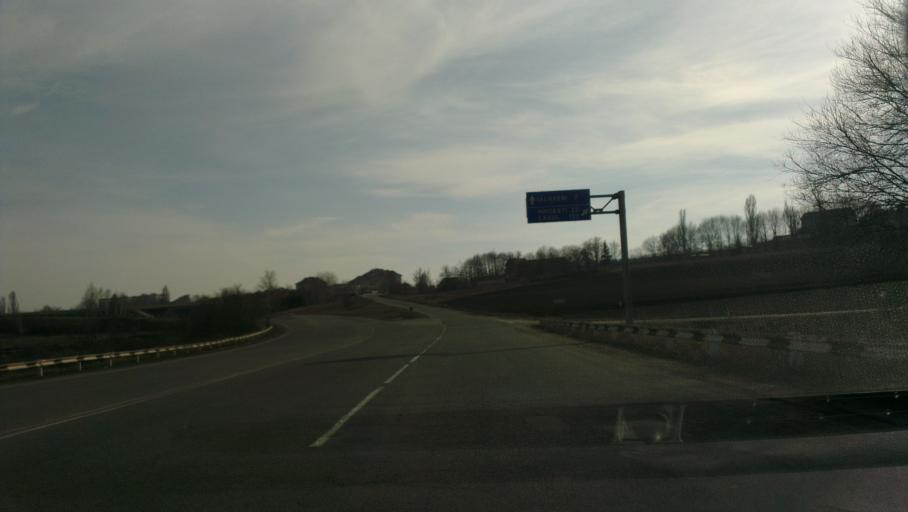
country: MD
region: Laloveni
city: Ialoveni
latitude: 46.9668
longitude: 28.7541
